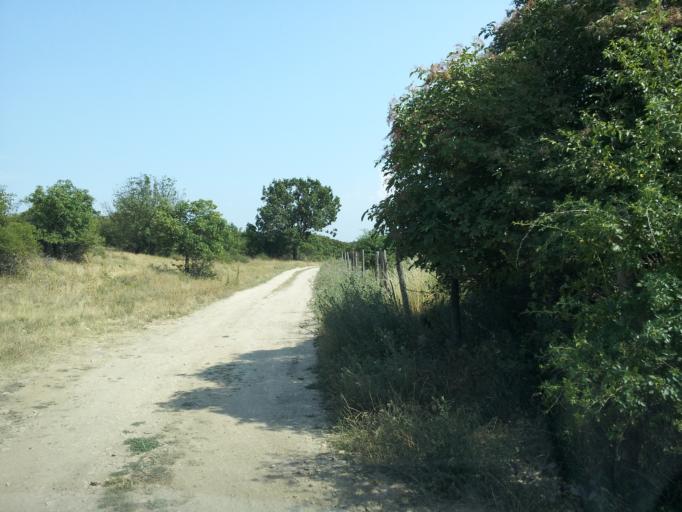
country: HU
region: Veszprem
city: Balatonfured
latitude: 46.9604
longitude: 17.8233
